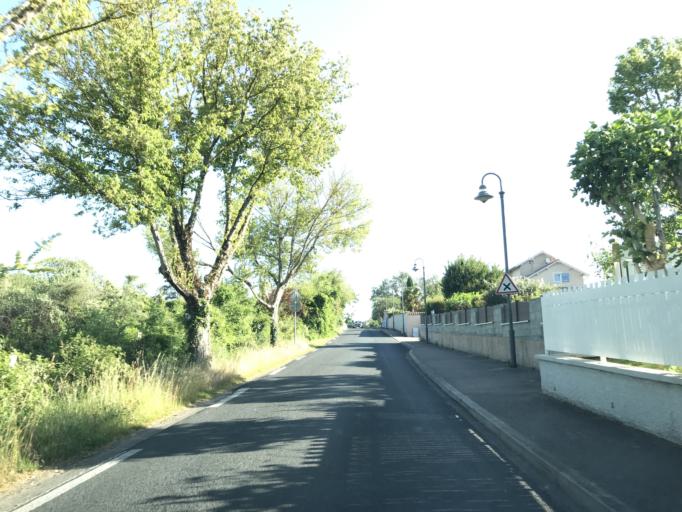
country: FR
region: Rhone-Alpes
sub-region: Departement du Rhone
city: Mions
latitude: 45.6586
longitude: 4.9579
